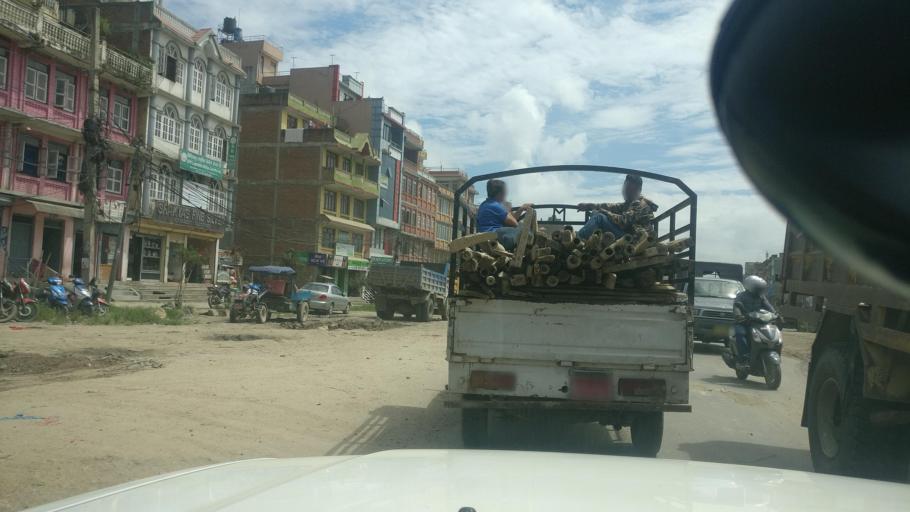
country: NP
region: Central Region
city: Banepa
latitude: 27.6320
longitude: 85.5148
